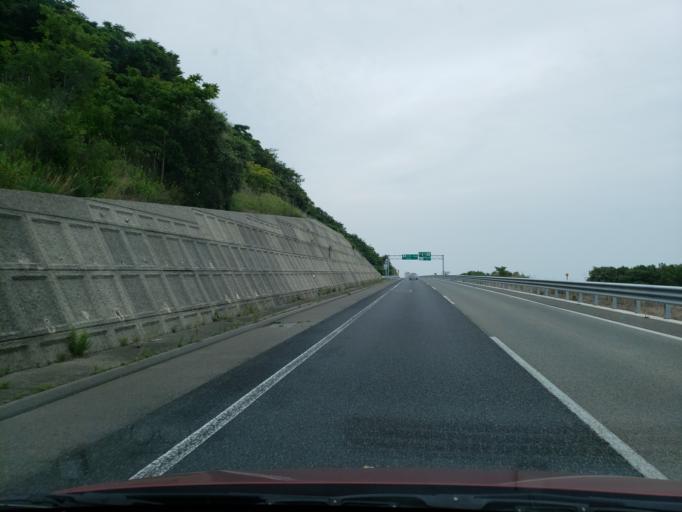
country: JP
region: Hyogo
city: Akashi
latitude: 34.5635
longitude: 135.0062
